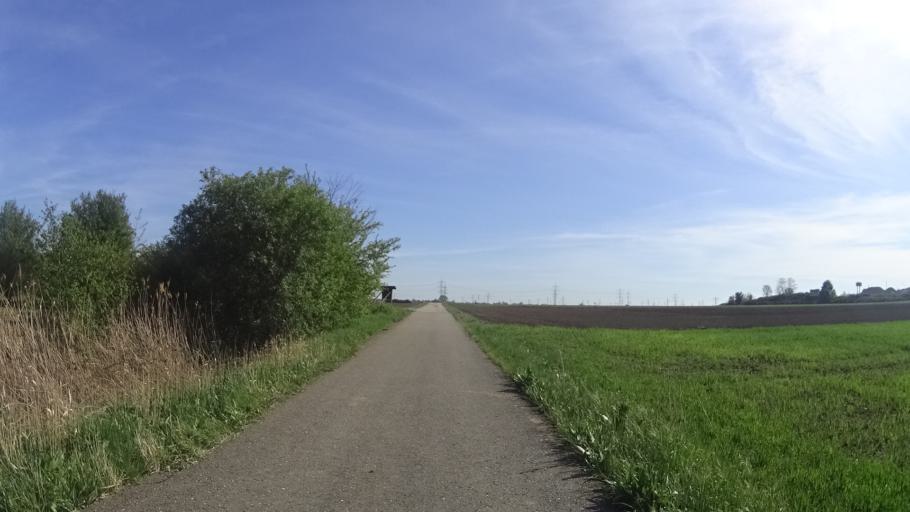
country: DE
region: Hesse
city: Viernheim
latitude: 49.5220
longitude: 8.5887
